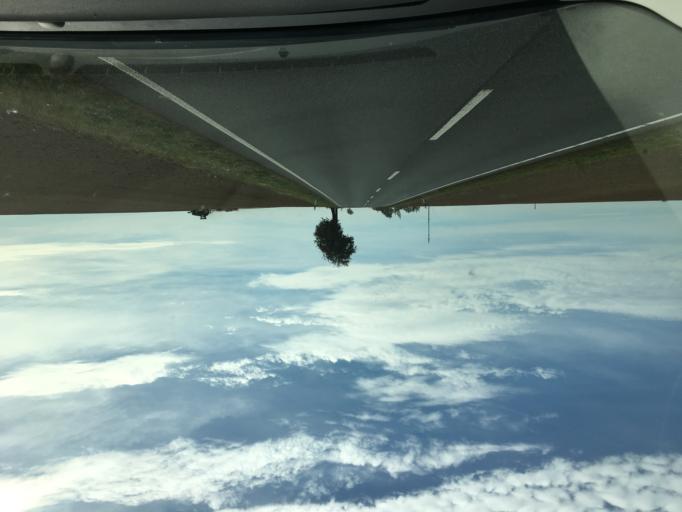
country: DE
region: Saxony
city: Lommatzsch
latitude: 51.2180
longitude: 13.3680
